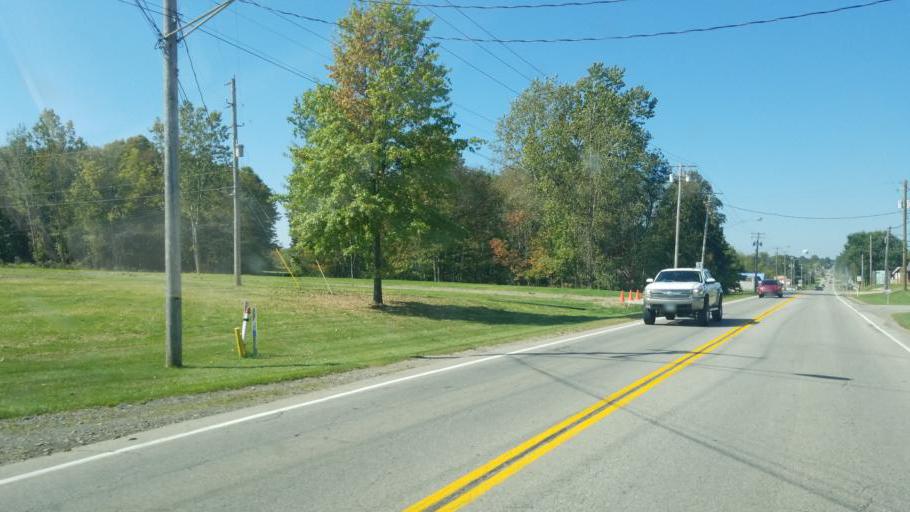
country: US
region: Ohio
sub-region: Richland County
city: Ontario
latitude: 40.7601
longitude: -82.6213
